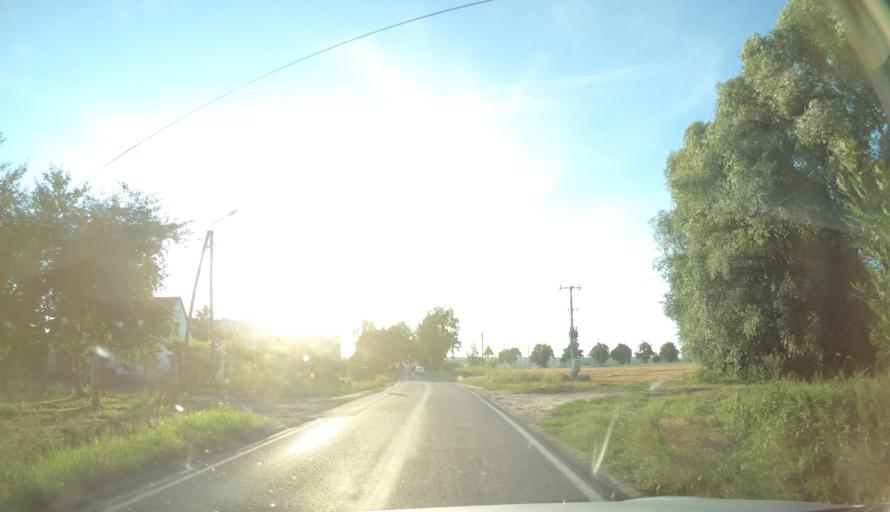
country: PL
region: Kujawsko-Pomorskie
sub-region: Powiat swiecki
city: Pruszcz
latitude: 53.2381
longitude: 18.2192
